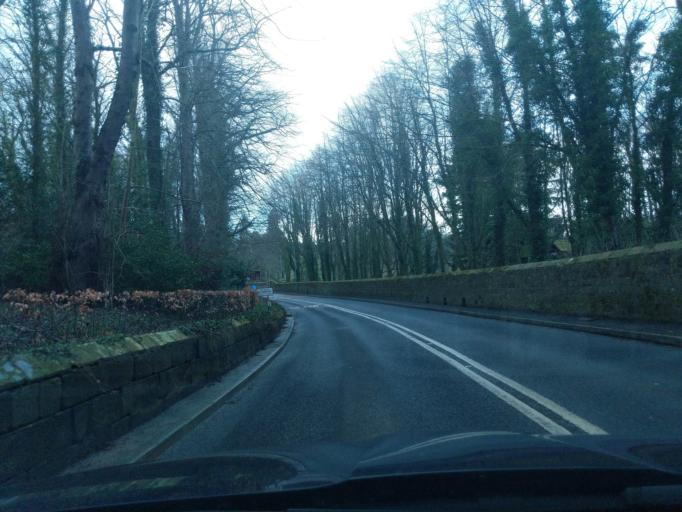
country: GB
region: England
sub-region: Northumberland
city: Alnwick
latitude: 55.4147
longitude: -1.6962
